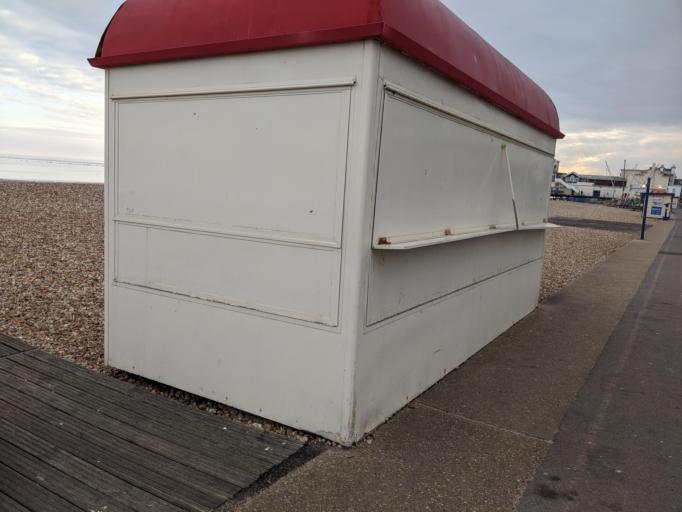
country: GB
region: England
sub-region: West Sussex
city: Bognor Regis
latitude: 50.7820
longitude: -0.6730
